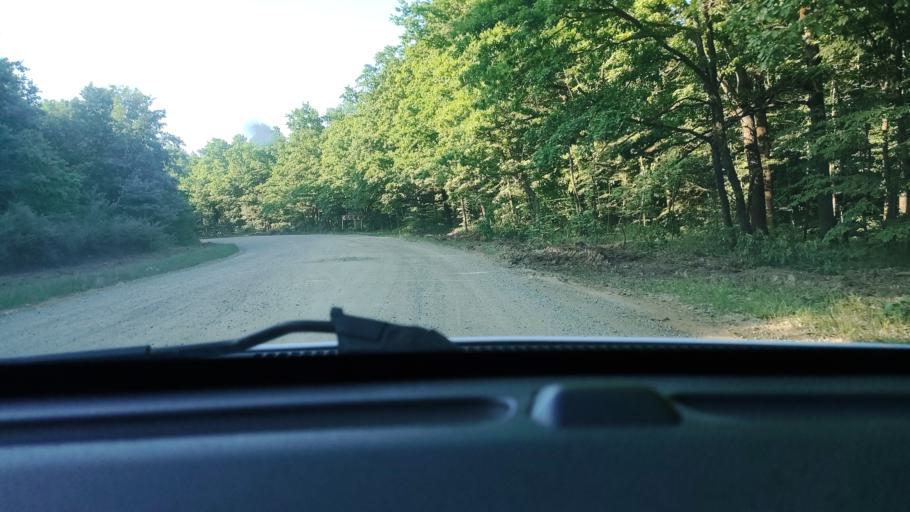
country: RU
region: Krasnodarskiy
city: Novodmitriyevskaya
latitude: 44.7174
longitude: 38.9917
